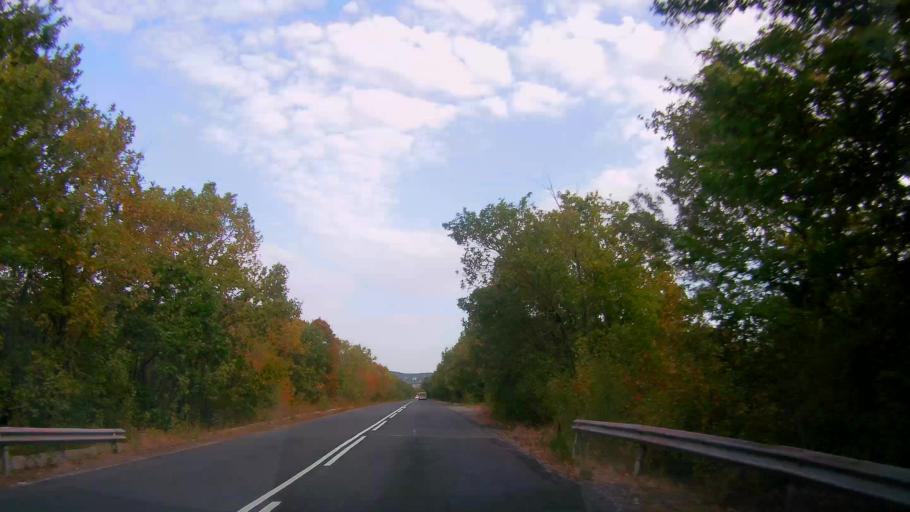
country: BG
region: Burgas
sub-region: Obshtina Sozopol
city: Sozopol
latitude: 42.3396
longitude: 27.7173
